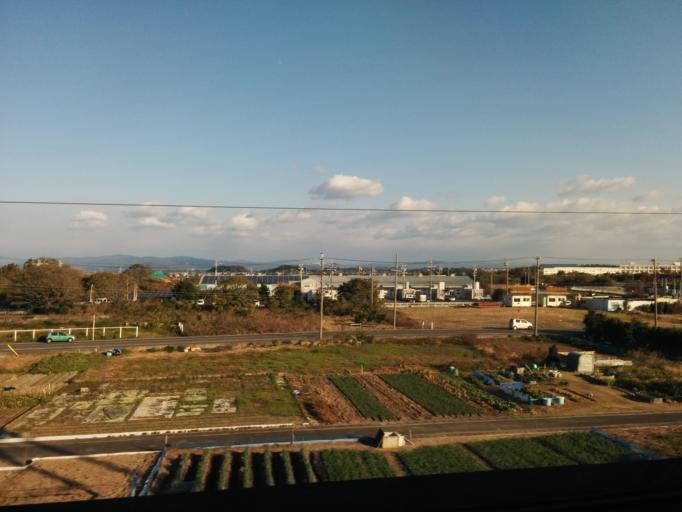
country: JP
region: Shizuoka
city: Kosai-shi
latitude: 34.6869
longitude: 137.6221
